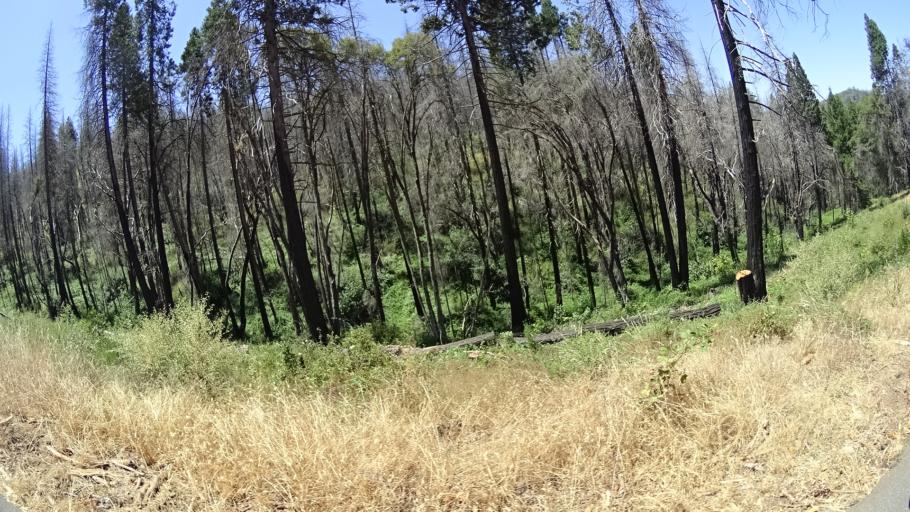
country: US
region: California
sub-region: Calaveras County
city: Mountain Ranch
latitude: 38.2553
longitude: -120.5804
